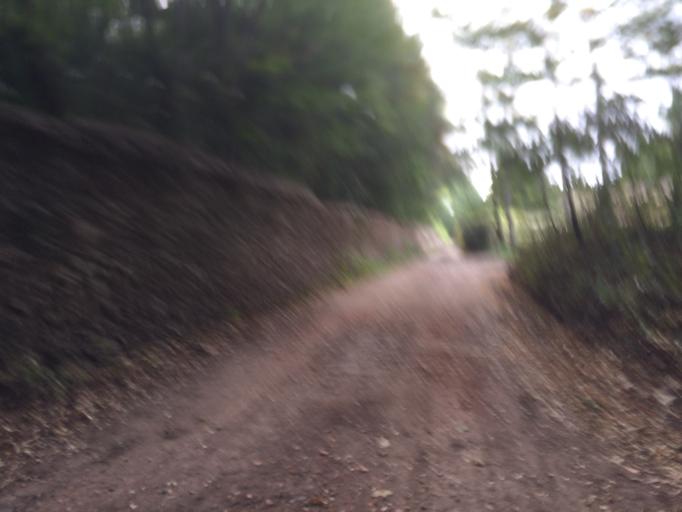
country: FR
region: Ile-de-France
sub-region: Departement des Yvelines
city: Bonnelles
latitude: 48.6148
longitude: 2.0152
